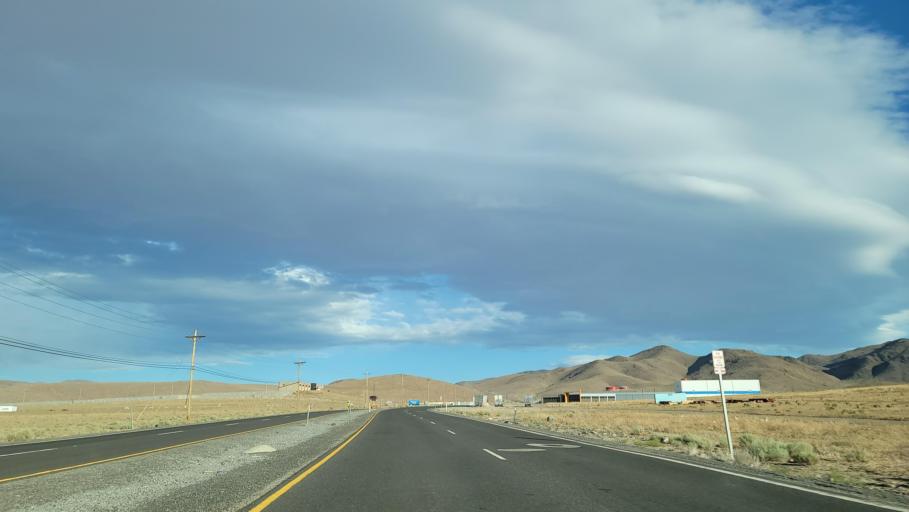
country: US
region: Nevada
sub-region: Lyon County
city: Stagecoach
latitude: 39.5360
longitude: -119.4858
